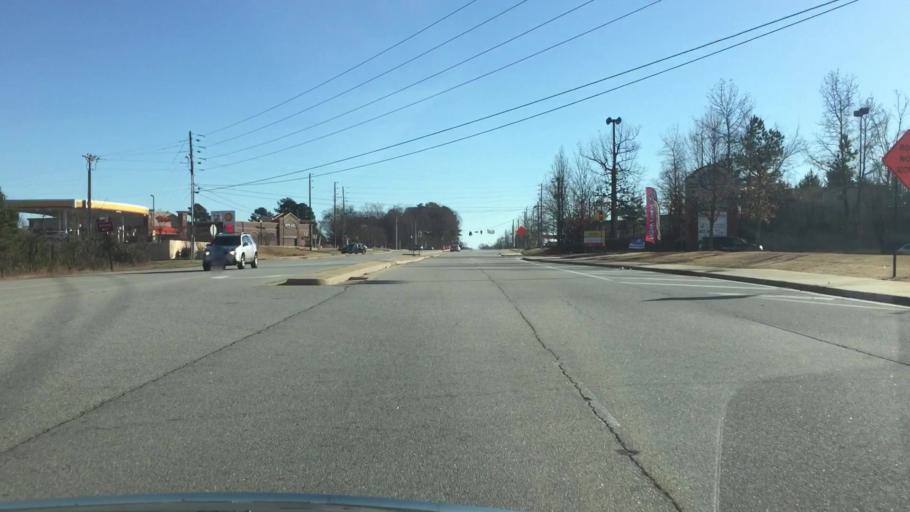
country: US
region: Georgia
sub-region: Henry County
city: McDonough
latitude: 33.5076
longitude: -84.1438
